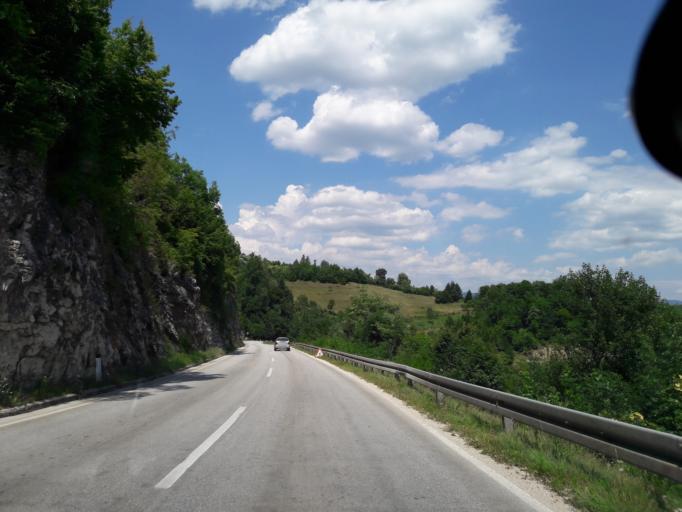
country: BA
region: Republika Srpska
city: Mrkonjic Grad
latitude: 44.4165
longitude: 17.0989
